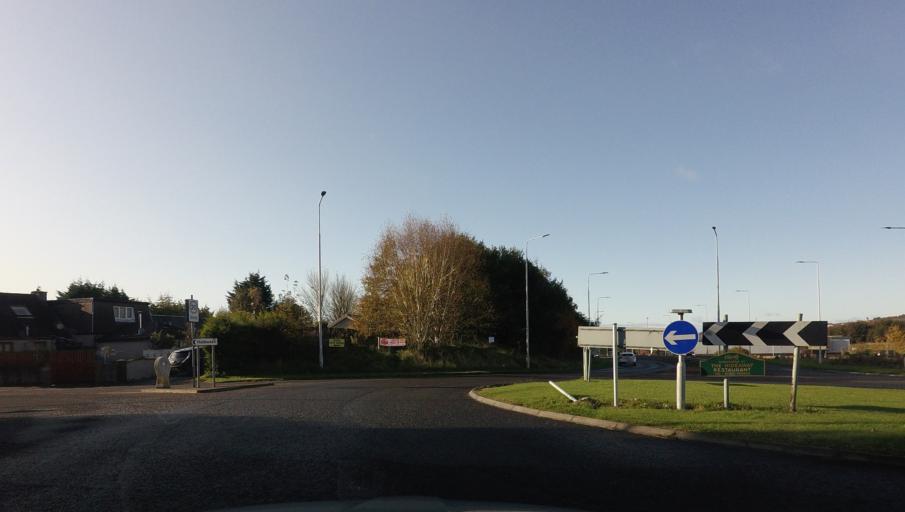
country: GB
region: Scotland
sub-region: Fife
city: Crossgates
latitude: 56.0820
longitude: -3.4032
